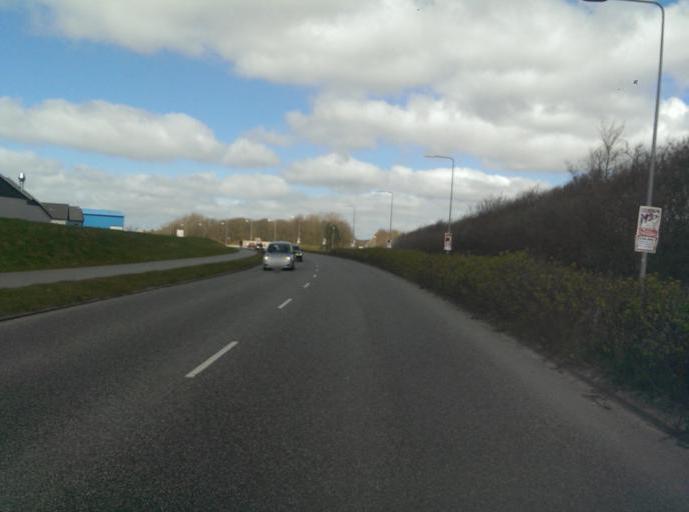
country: DK
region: South Denmark
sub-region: Esbjerg Kommune
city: Esbjerg
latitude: 55.4824
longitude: 8.4258
